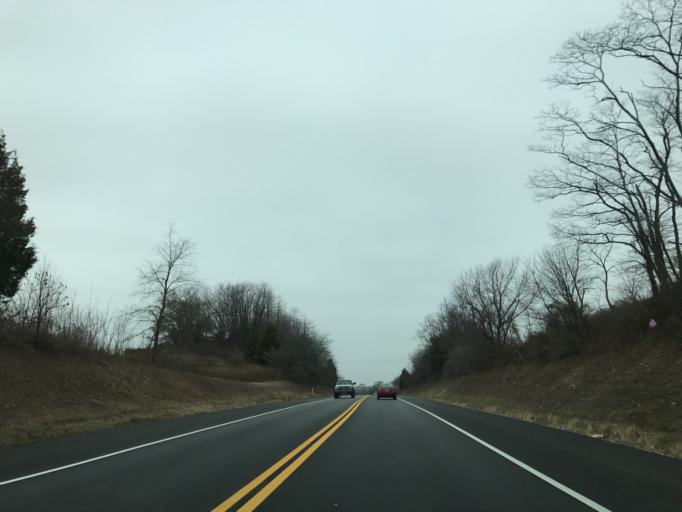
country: US
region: Maryland
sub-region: Carroll County
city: New Windsor
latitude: 39.6105
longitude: -77.0733
